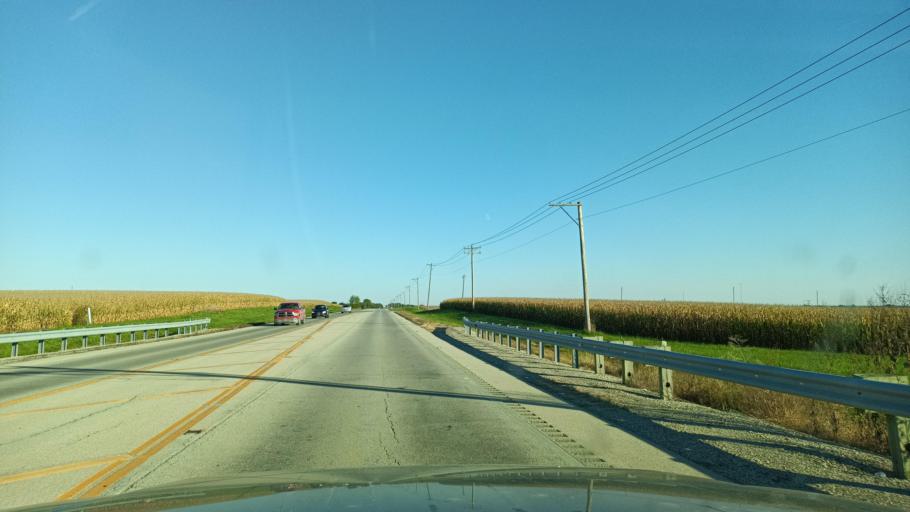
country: US
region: Illinois
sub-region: Champaign County
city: Lake of the Woods
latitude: 40.1786
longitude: -88.3529
